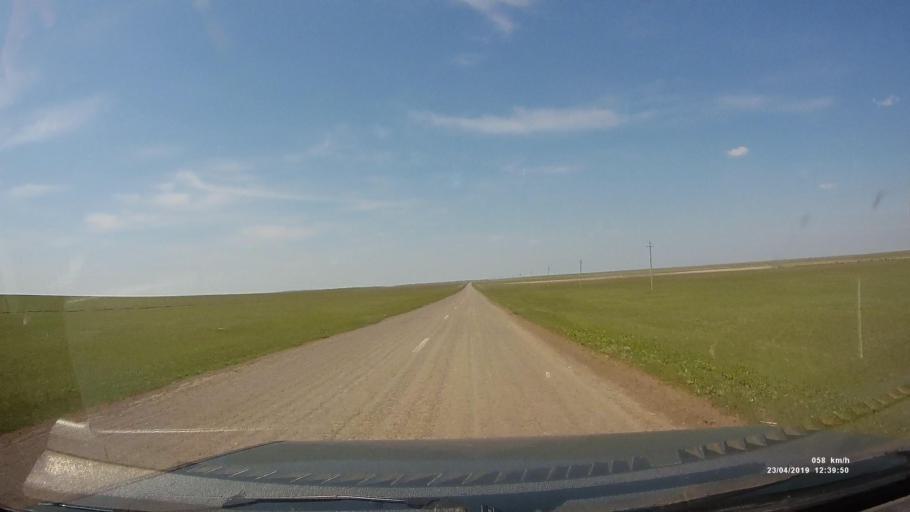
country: RU
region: Kalmykiya
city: Yashalta
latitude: 46.4364
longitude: 42.7045
